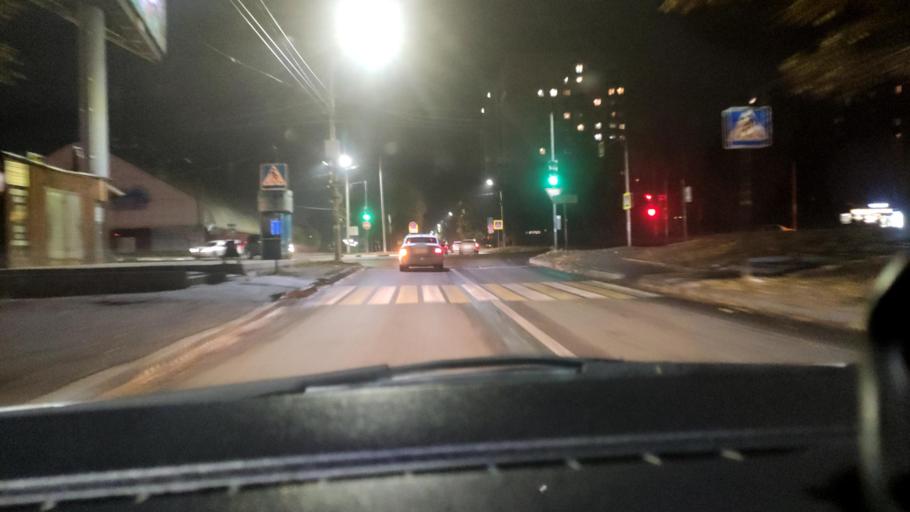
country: RU
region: Voronezj
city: Podgornoye
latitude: 51.7056
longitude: 39.1631
